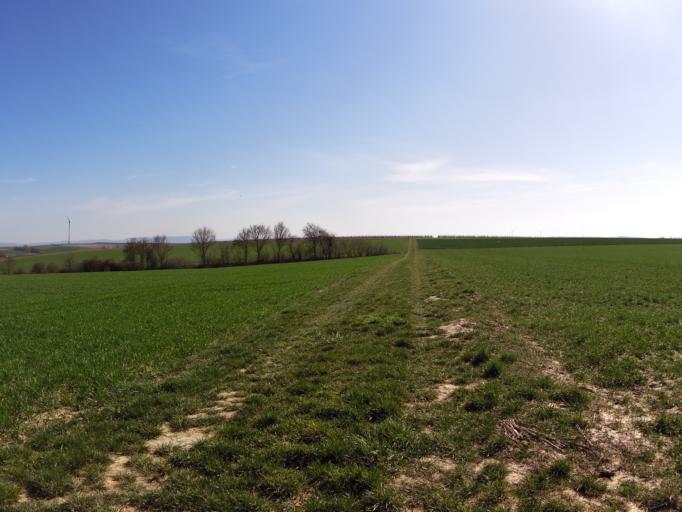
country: DE
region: Bavaria
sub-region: Regierungsbezirk Unterfranken
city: Prosselsheim
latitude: 49.8490
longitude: 10.1288
